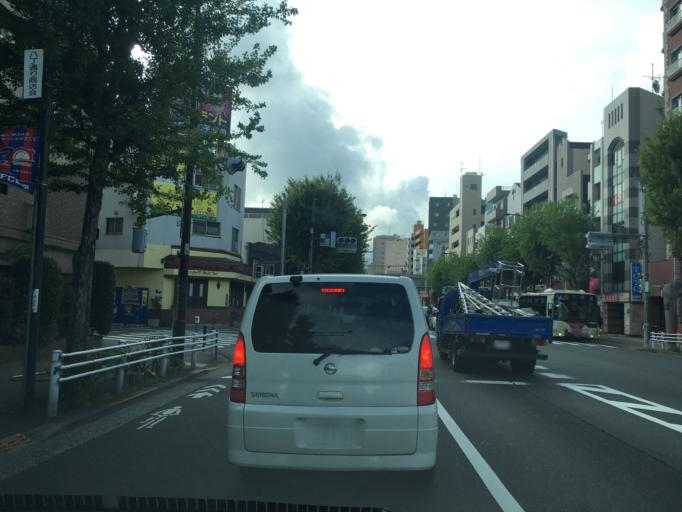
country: JP
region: Tokyo
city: Musashino
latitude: 35.7079
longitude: 139.6154
